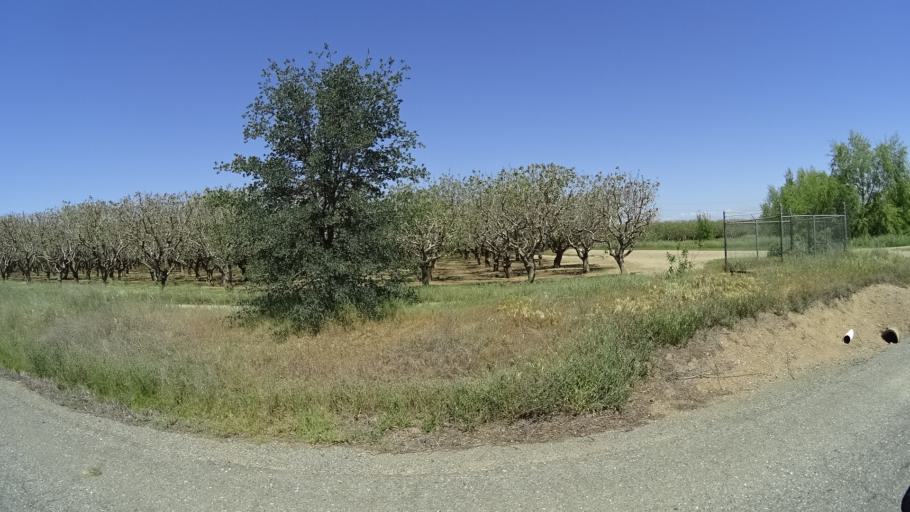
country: US
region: California
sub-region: Glenn County
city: Orland
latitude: 39.7795
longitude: -122.1472
